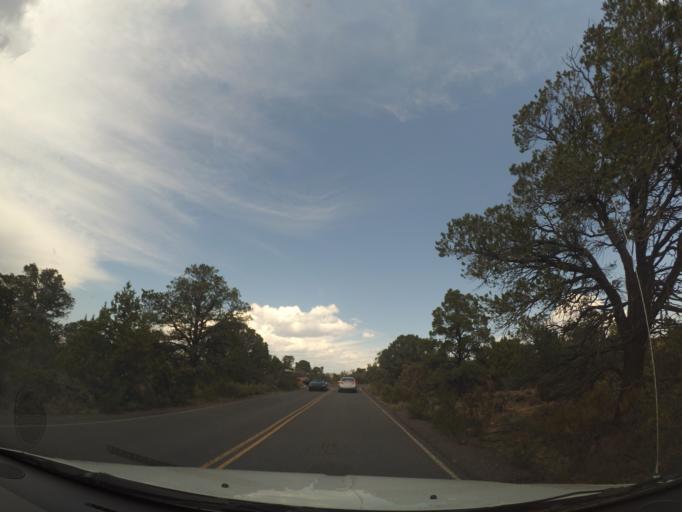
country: US
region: Arizona
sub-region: Coconino County
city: Grand Canyon
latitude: 36.0039
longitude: -111.9238
